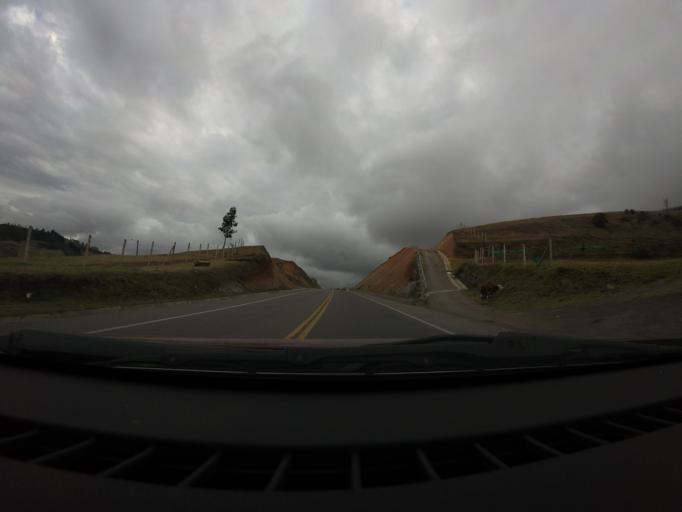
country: CO
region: Boyaca
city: Tunja
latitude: 5.5022
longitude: -73.3783
